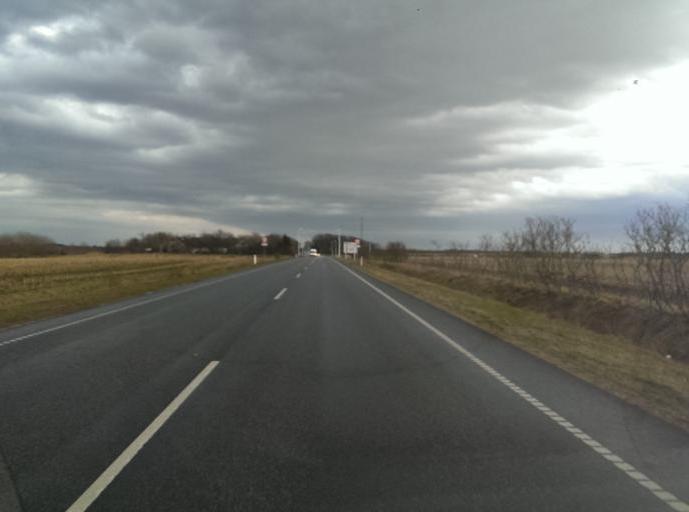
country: DK
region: South Denmark
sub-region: Esbjerg Kommune
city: Tjaereborg
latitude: 55.4969
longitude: 8.6191
